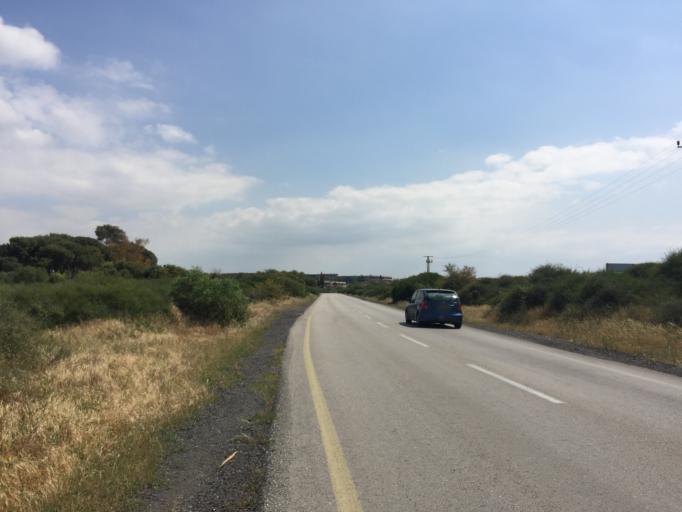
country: IL
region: Haifa
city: Qesarya
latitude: 32.4935
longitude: 34.8982
